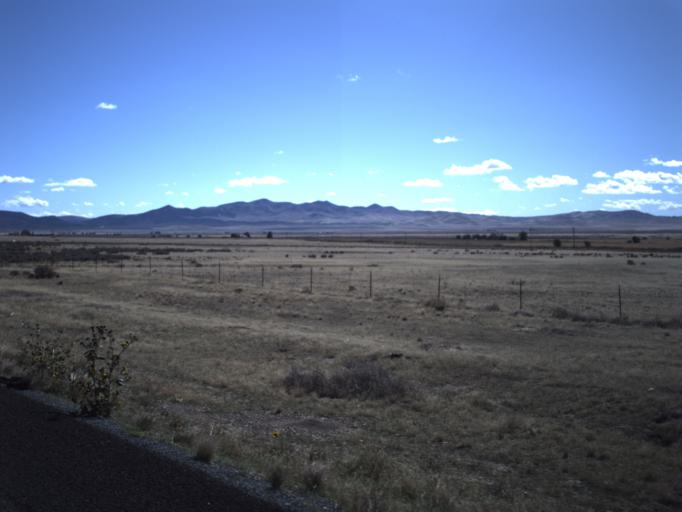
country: US
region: Utah
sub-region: Beaver County
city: Milford
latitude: 38.2767
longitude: -112.9610
